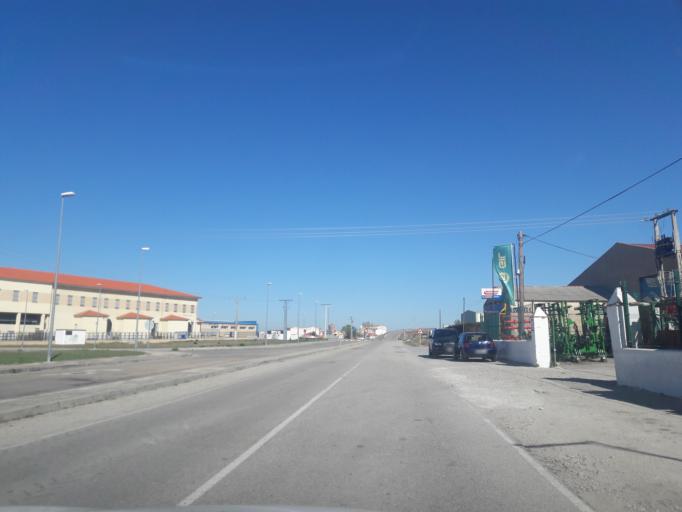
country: ES
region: Castille and Leon
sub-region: Provincia de Salamanca
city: Penaranda de Bracamonte
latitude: 40.8917
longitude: -5.1981
